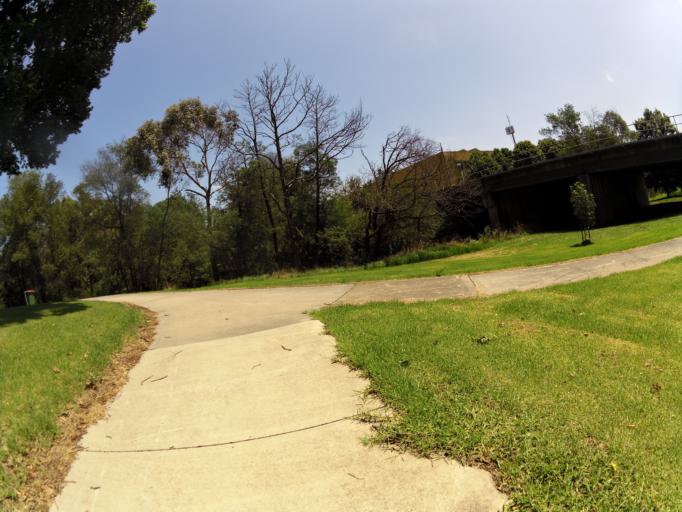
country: AU
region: Victoria
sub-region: Latrobe
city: Traralgon
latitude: -38.1980
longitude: 146.5425
